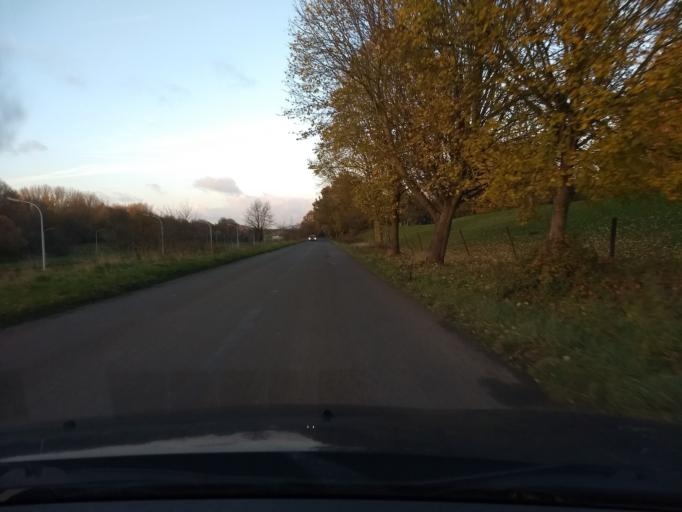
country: BE
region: Wallonia
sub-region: Province du Brabant Wallon
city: Ittre
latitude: 50.6111
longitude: 4.2257
